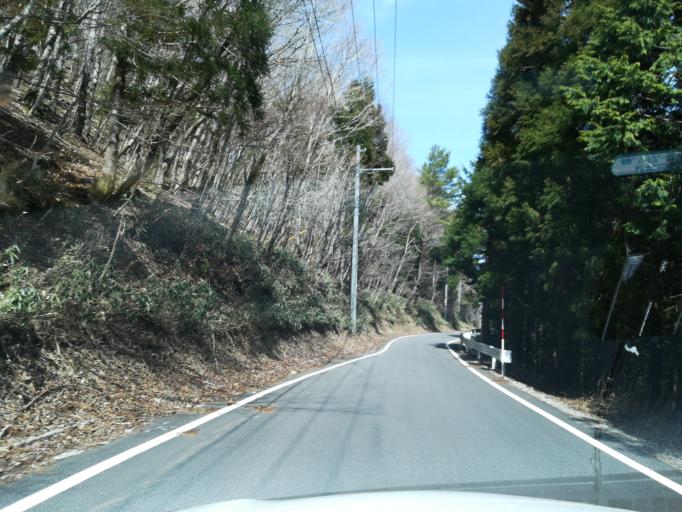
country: JP
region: Tokushima
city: Wakimachi
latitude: 33.8752
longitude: 134.0586
